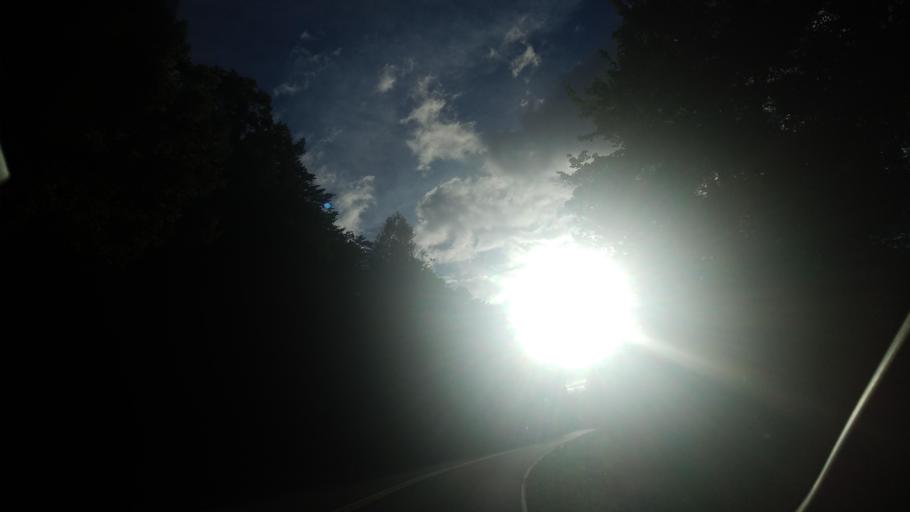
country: US
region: Tennessee
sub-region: Cocke County
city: Newport
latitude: 35.8096
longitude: -83.2311
